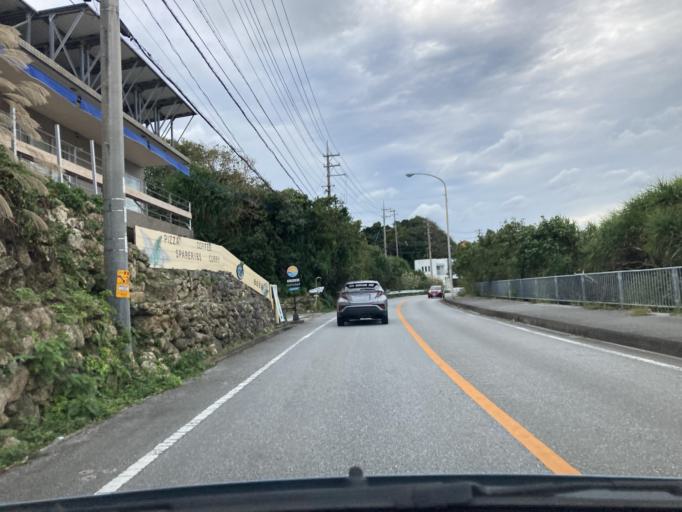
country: JP
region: Okinawa
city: Ishikawa
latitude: 26.4347
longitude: 127.7865
